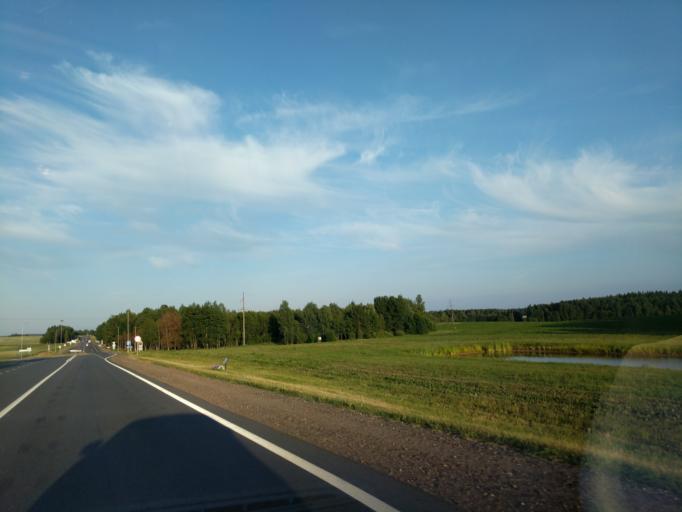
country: BY
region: Minsk
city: Bal'shavik
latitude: 54.0902
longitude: 27.5314
